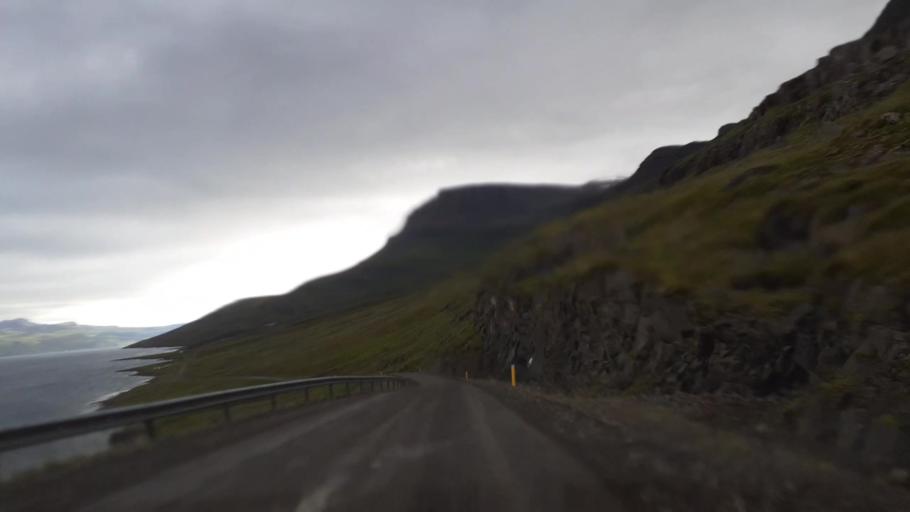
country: IS
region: East
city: Reydarfjoerdur
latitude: 65.0127
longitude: -14.1824
